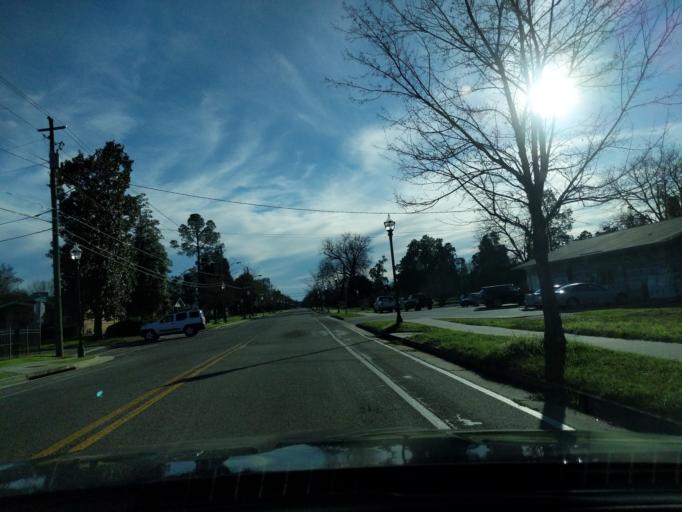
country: US
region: Georgia
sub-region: Richmond County
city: Augusta
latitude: 33.4648
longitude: -81.9502
